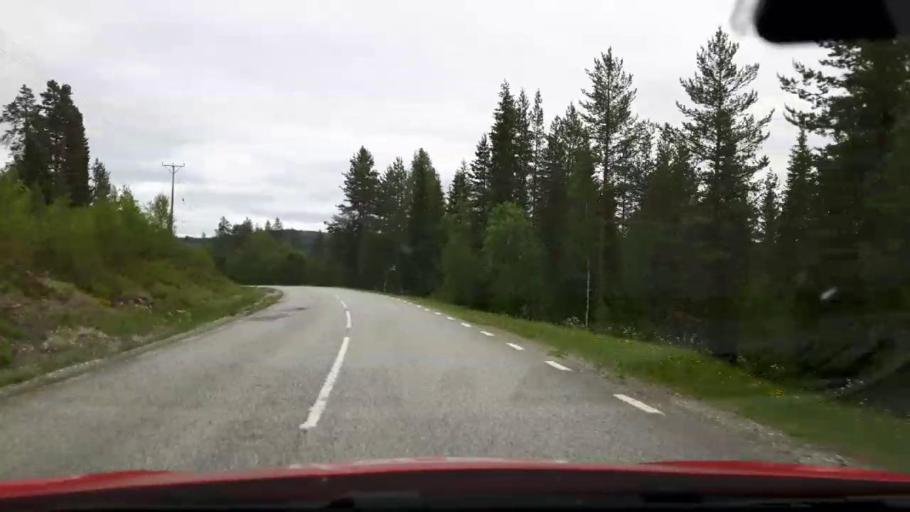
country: SE
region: Jaemtland
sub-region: Stroemsunds Kommun
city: Stroemsund
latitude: 63.2934
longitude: 15.7709
